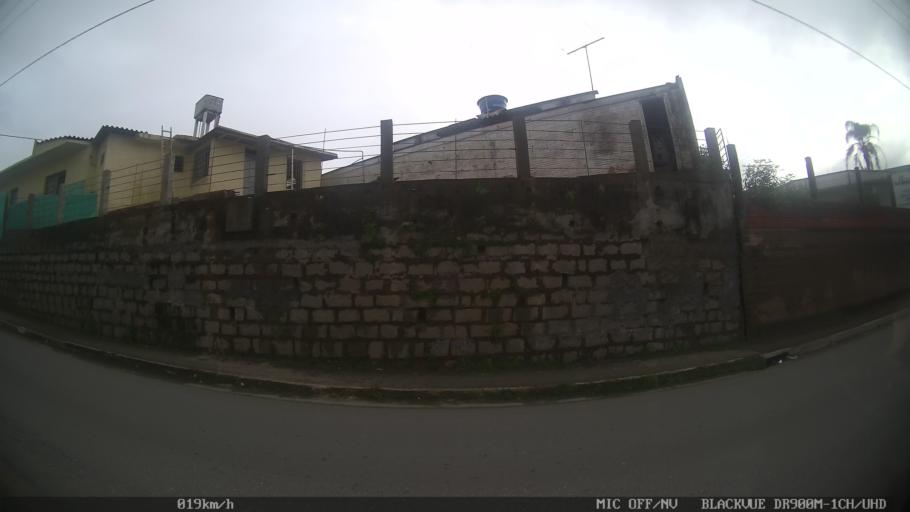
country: BR
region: Santa Catarina
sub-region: Sao Jose
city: Campinas
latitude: -27.5893
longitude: -48.6211
